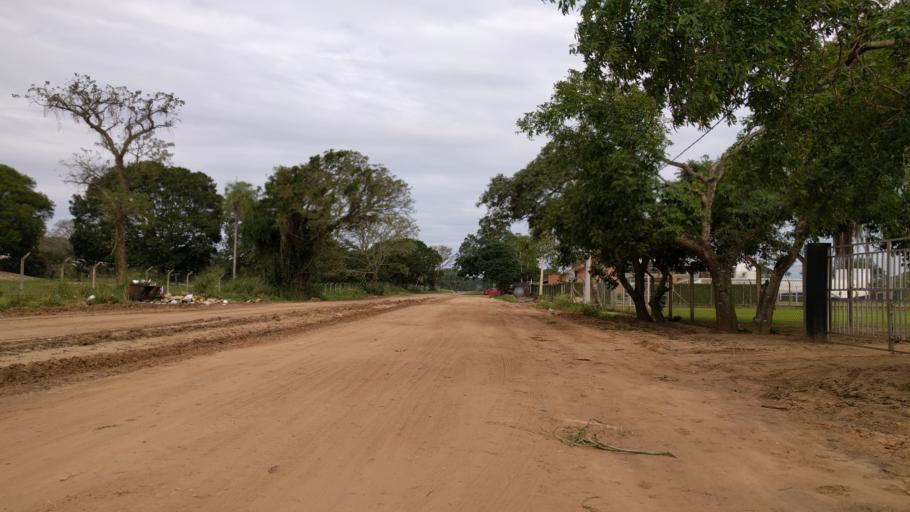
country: BO
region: Santa Cruz
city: Santa Cruz de la Sierra
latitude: -17.8130
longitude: -63.2355
